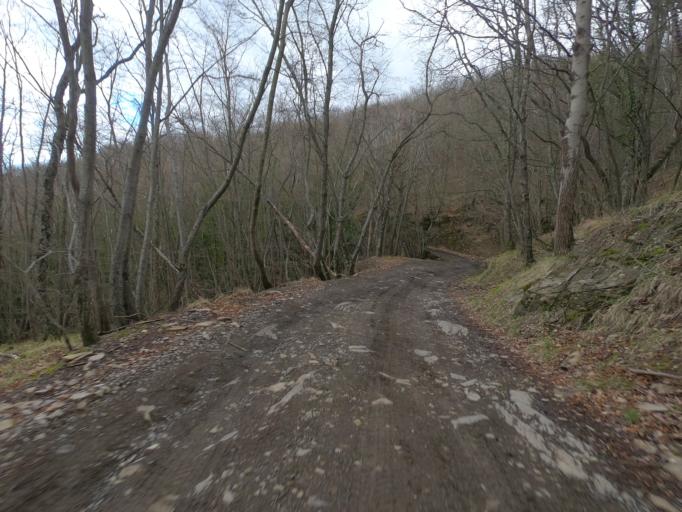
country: IT
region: Liguria
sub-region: Provincia di Imperia
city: Pietrabruna
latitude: 43.9132
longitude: 7.8868
